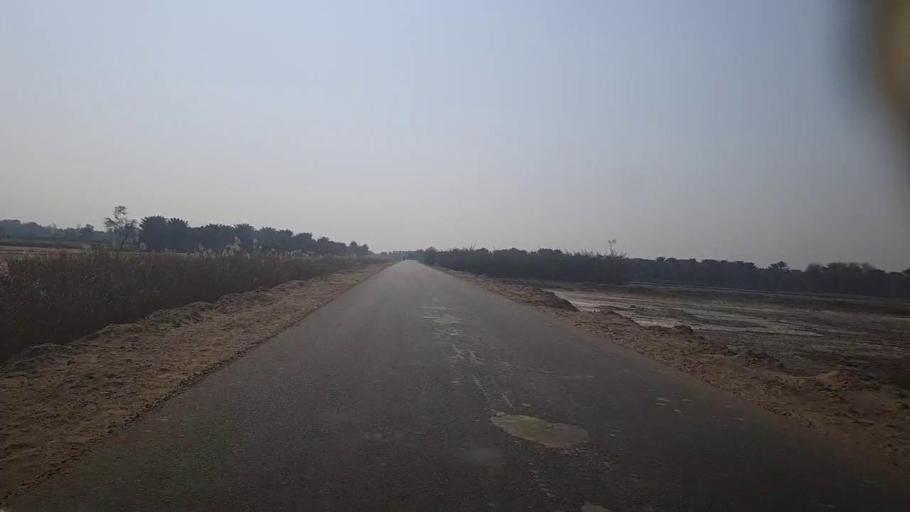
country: PK
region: Sindh
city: Khairpur
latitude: 27.4700
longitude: 68.8207
